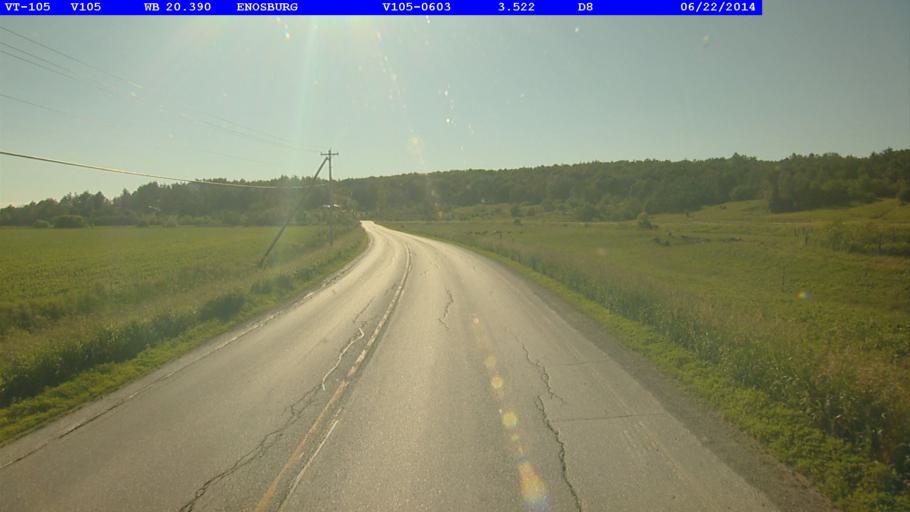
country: US
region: Vermont
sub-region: Franklin County
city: Enosburg Falls
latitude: 44.9207
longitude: -72.7584
